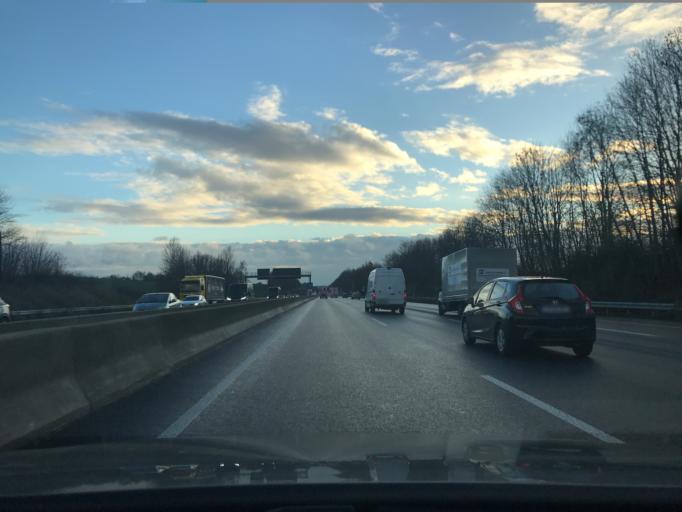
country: DE
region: North Rhine-Westphalia
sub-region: Regierungsbezirk Dusseldorf
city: Erkrath
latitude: 51.2568
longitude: 6.9142
